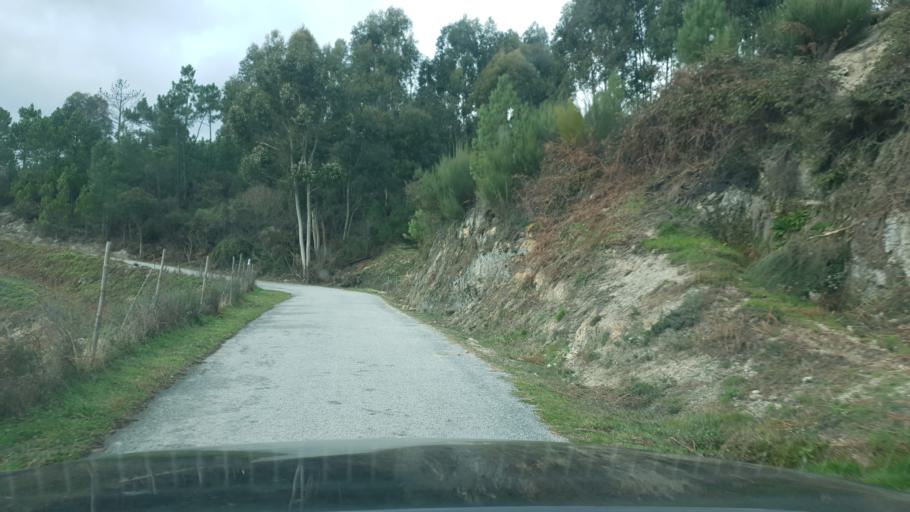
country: PT
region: Viseu
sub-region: Castro Daire
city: Castro Daire
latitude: 40.8805
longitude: -8.0031
